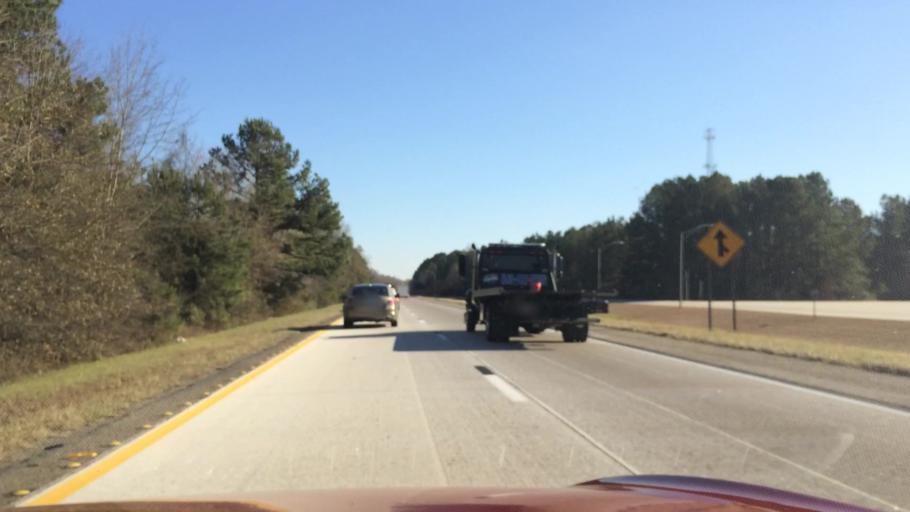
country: US
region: South Carolina
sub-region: Orangeburg County
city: Holly Hill
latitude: 33.2694
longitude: -80.4871
